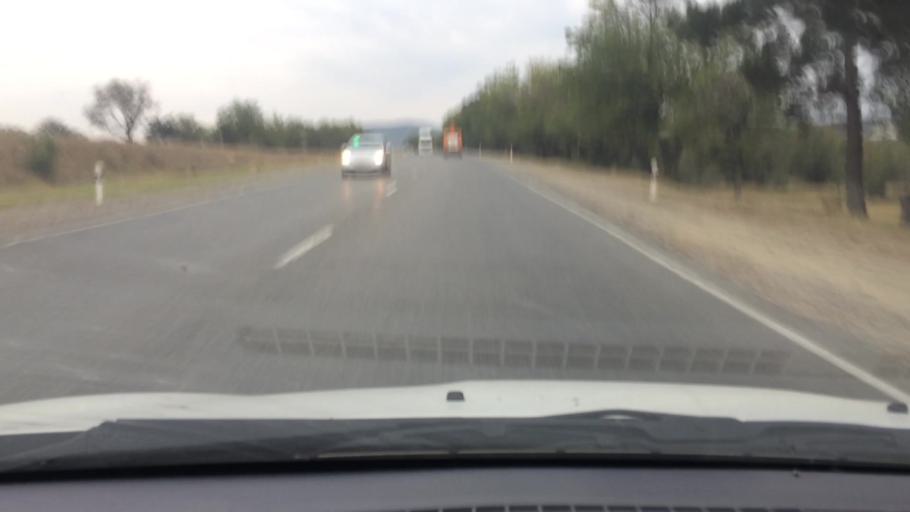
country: GE
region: T'bilisi
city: Tbilisi
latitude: 41.6403
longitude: 44.8656
